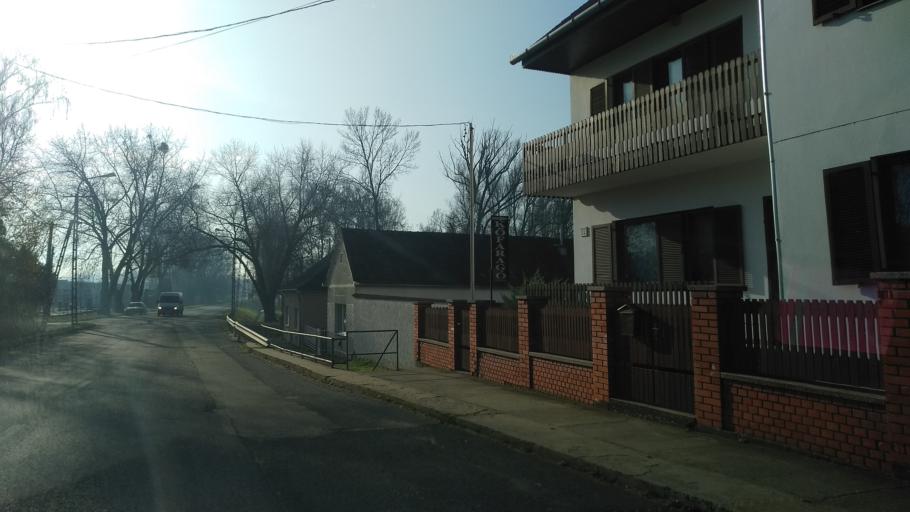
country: HU
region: Somogy
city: Barcs
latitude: 45.9570
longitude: 17.4634
